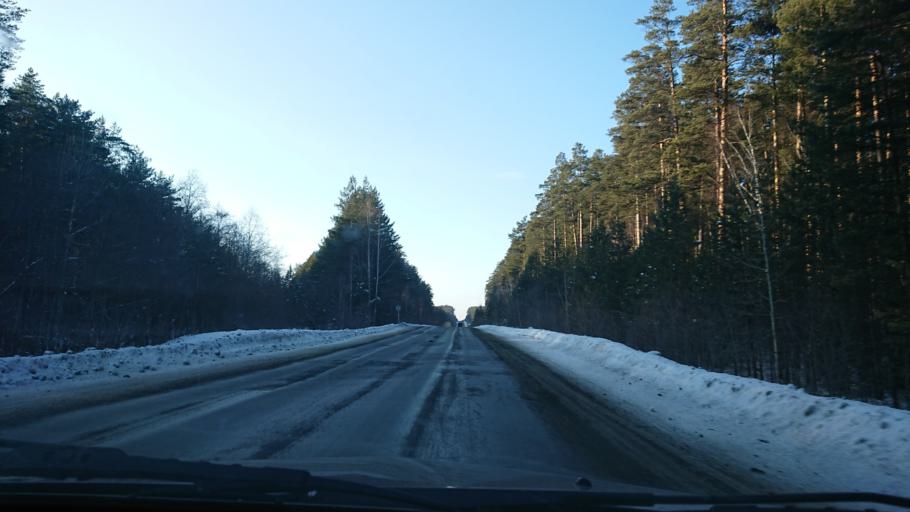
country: RU
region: Sverdlovsk
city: Gornyy Shchit
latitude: 56.6309
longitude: 60.3315
